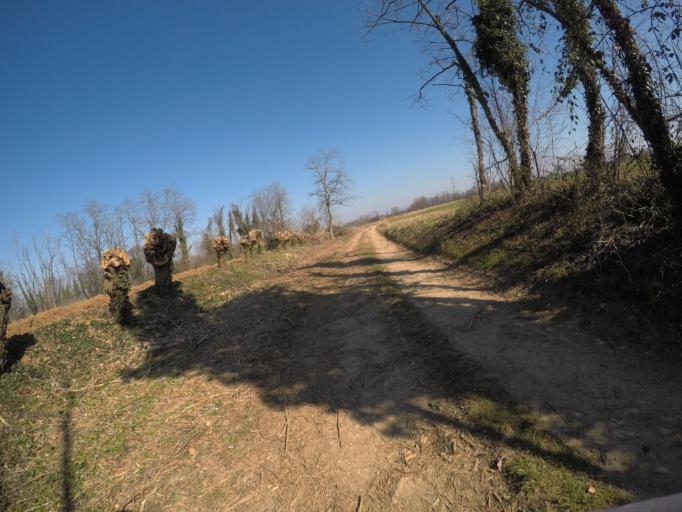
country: IT
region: Friuli Venezia Giulia
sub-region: Provincia di Udine
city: Lestizza
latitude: 45.9779
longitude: 13.1610
